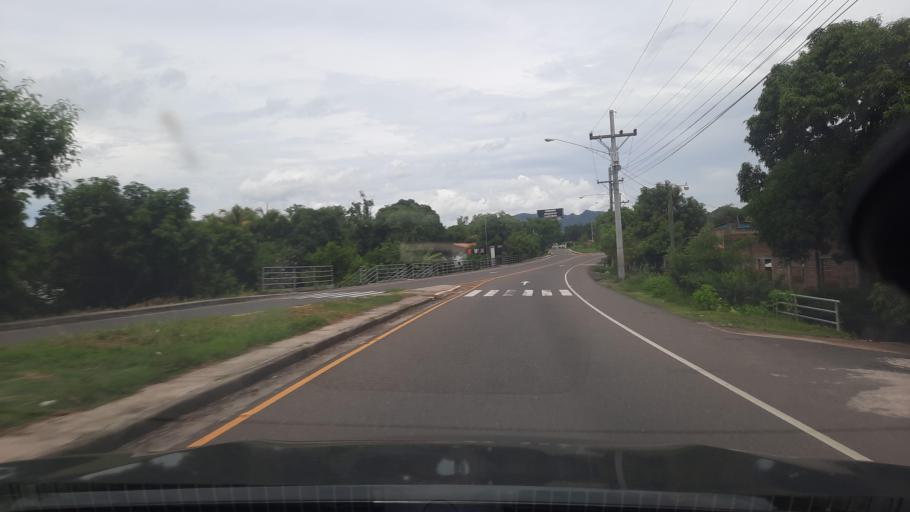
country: HN
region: Valle
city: Jicaro Galan
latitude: 13.5309
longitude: -87.4406
